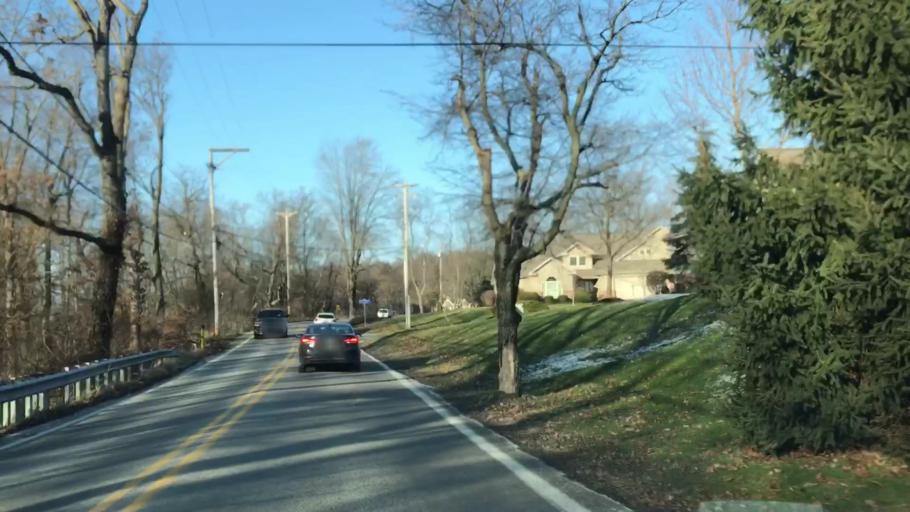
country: US
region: Pennsylvania
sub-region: Allegheny County
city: Gibsonia
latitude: 40.6018
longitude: -79.9772
